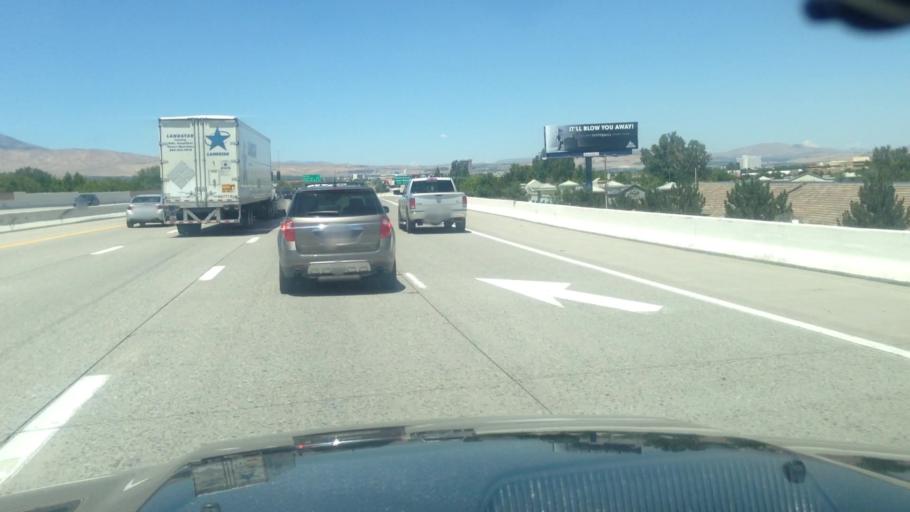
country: US
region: Nevada
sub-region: Washoe County
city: Reno
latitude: 39.4543
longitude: -119.7814
